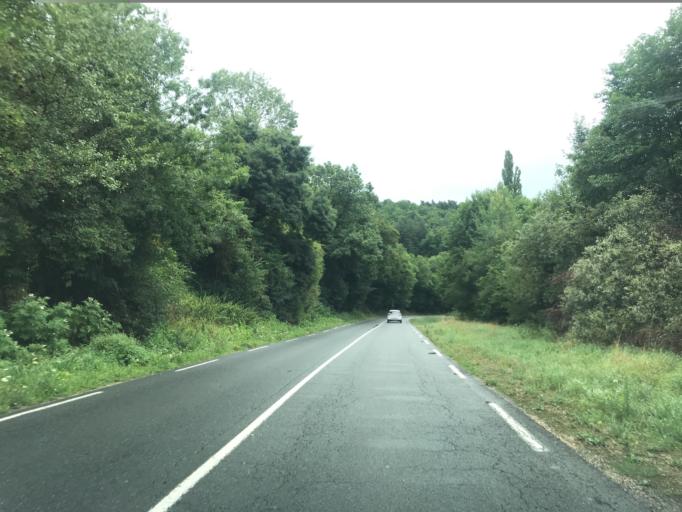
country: FR
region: Aquitaine
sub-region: Departement de la Dordogne
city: Chancelade
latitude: 45.2142
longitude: 0.6725
